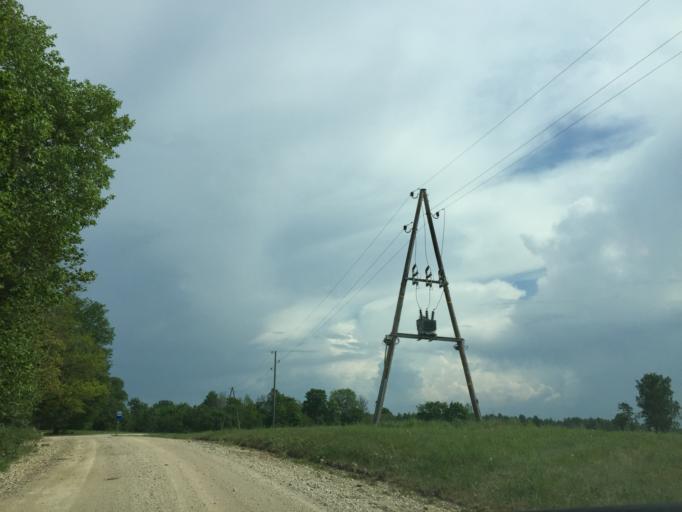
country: LV
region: Livani
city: Livani
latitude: 56.5849
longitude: 26.2126
